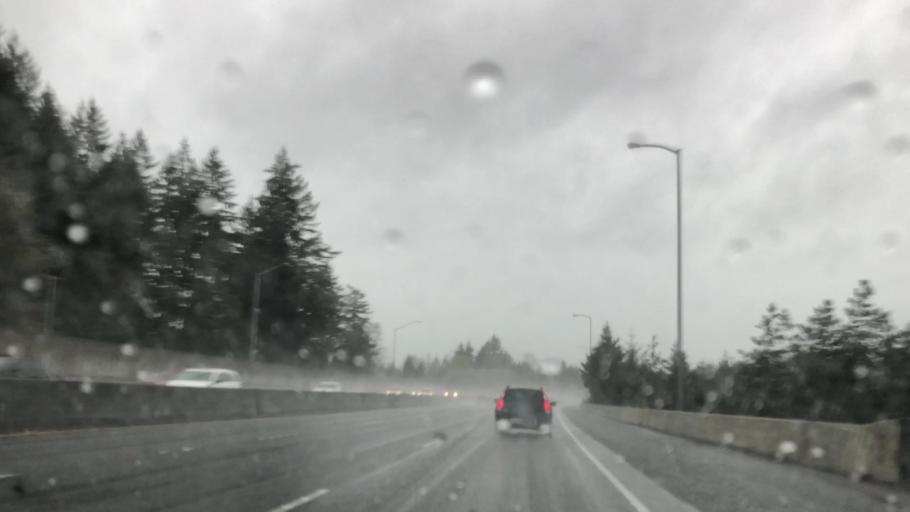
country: US
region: Oregon
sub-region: Washington County
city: West Slope
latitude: 45.5060
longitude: -122.7559
